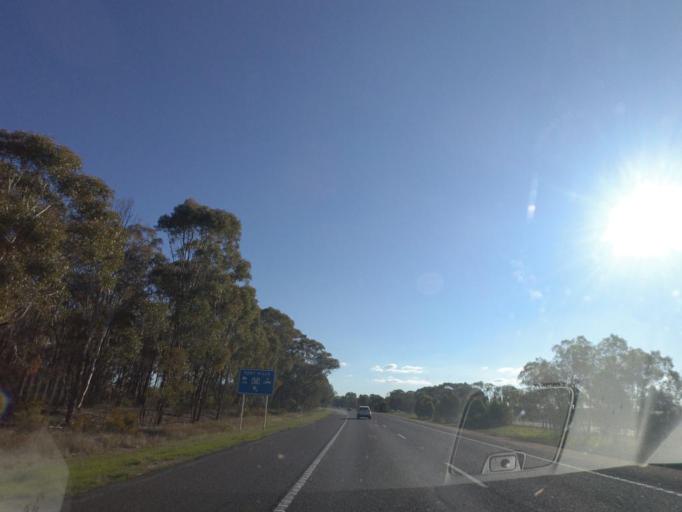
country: AU
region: Victoria
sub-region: Benalla
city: Benalla
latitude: -36.5763
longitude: 145.9257
